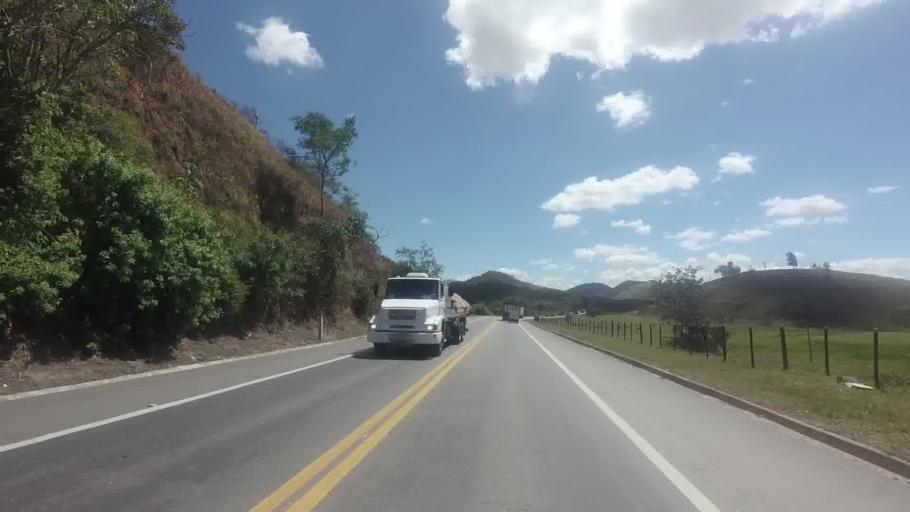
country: BR
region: Espirito Santo
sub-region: Viana
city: Viana
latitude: -20.4164
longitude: -40.4600
